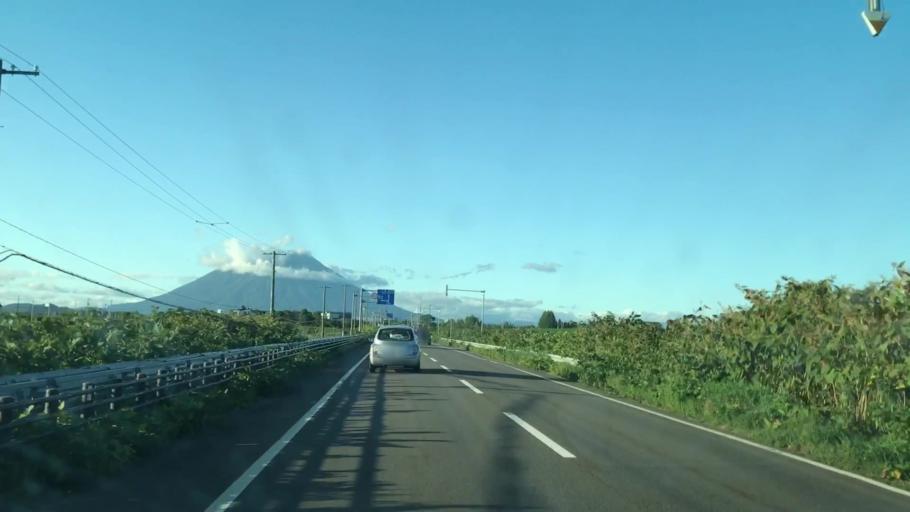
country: JP
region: Hokkaido
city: Niseko Town
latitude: 42.6582
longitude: 140.8115
